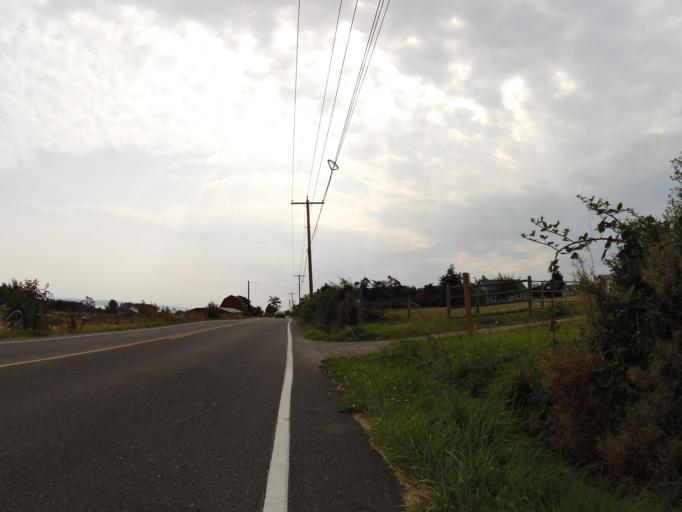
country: US
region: Washington
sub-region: Island County
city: Coupeville
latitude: 48.1916
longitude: -122.6682
